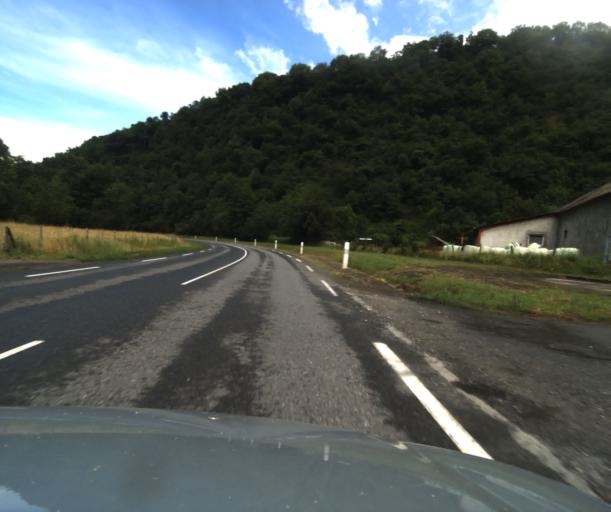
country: FR
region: Midi-Pyrenees
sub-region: Departement des Hautes-Pyrenees
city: Pierrefitte-Nestalas
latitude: 42.9648
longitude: -0.0609
